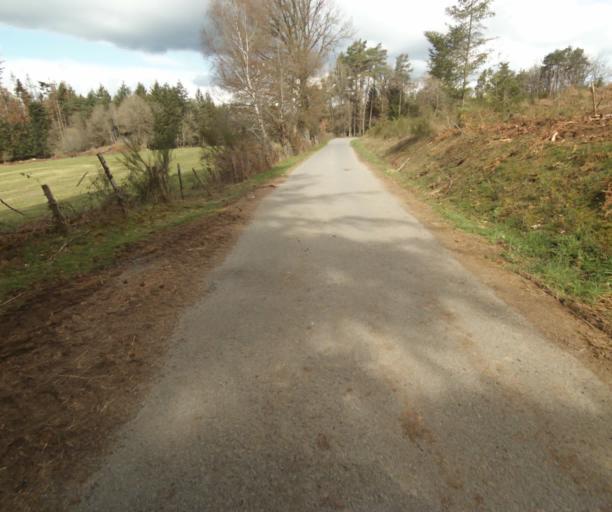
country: FR
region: Limousin
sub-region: Departement de la Correze
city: Correze
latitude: 45.3904
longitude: 1.9136
